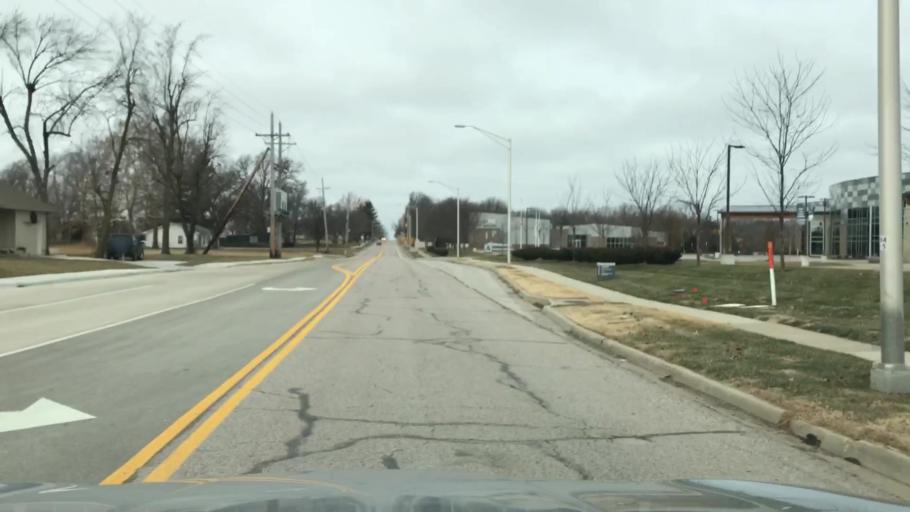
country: US
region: Missouri
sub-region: Jackson County
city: Lees Summit
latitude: 38.8962
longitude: -94.3775
